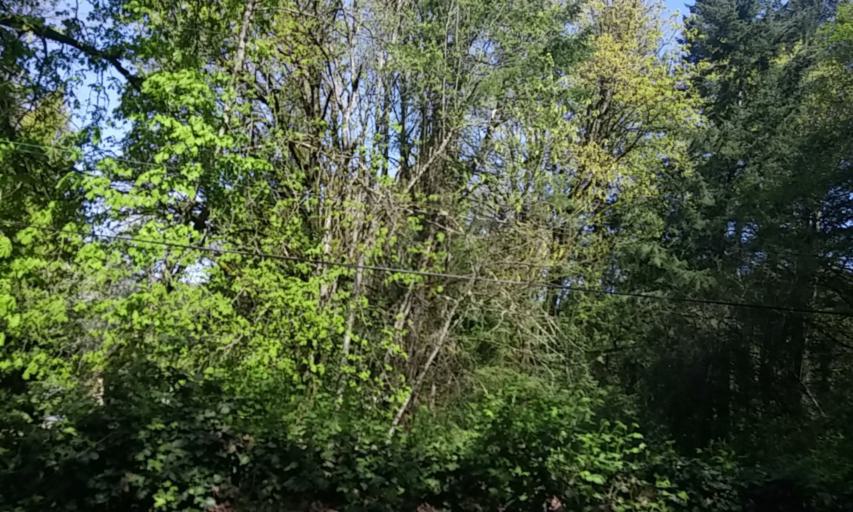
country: US
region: Oregon
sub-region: Washington County
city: West Haven-Sylvan
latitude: 45.5195
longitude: -122.7618
